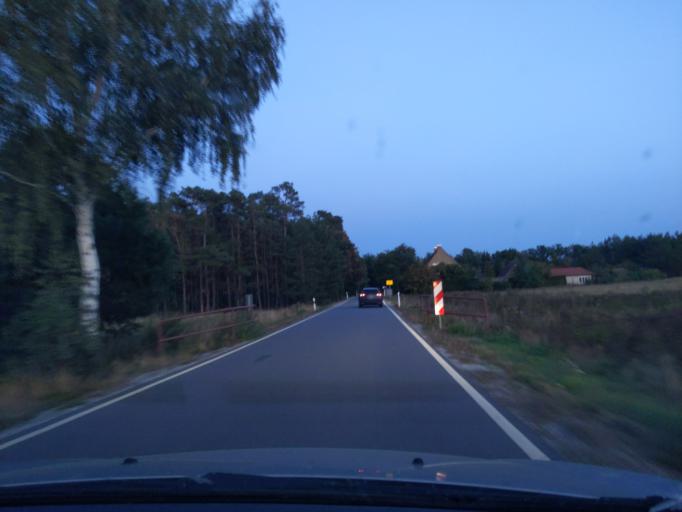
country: DE
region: Saxony
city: Lohsa
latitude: 51.3286
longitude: 14.4008
